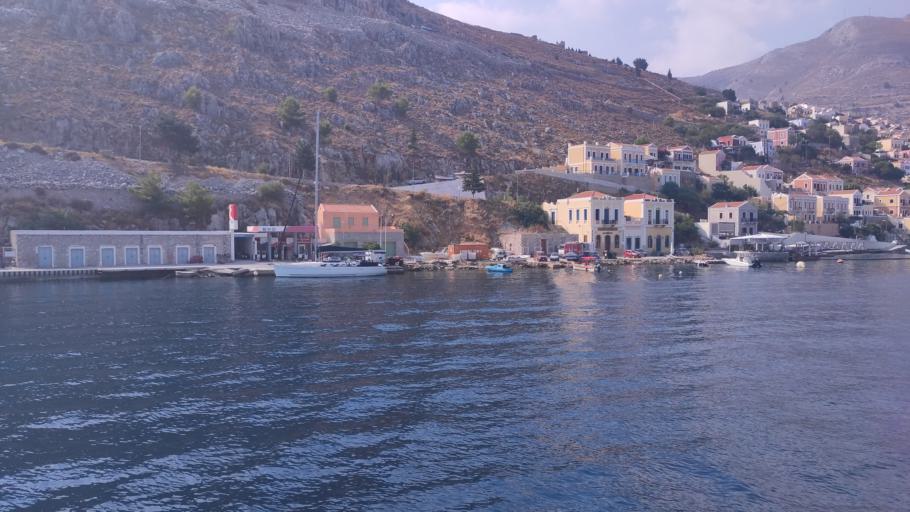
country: GR
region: South Aegean
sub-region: Nomos Dodekanisou
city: Symi
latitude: 36.6198
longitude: 27.8435
